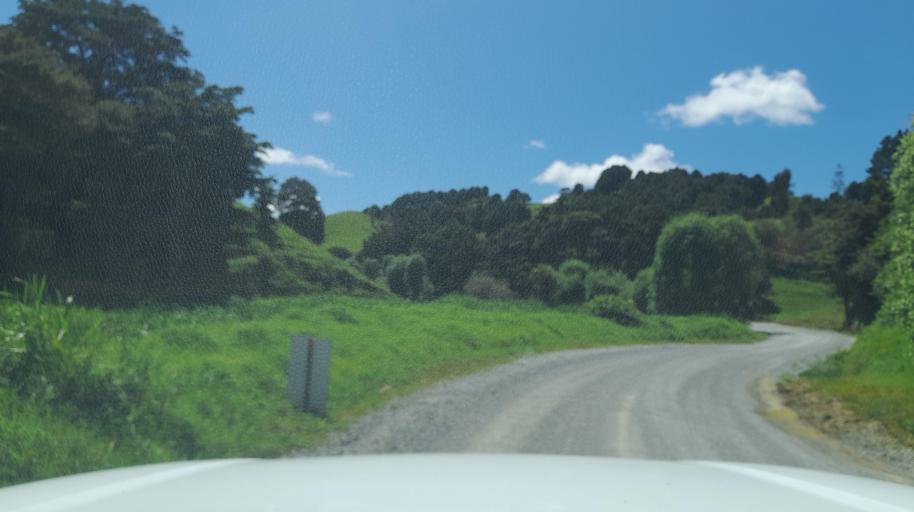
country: NZ
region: Northland
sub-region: Far North District
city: Taipa
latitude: -35.1219
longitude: 173.4065
